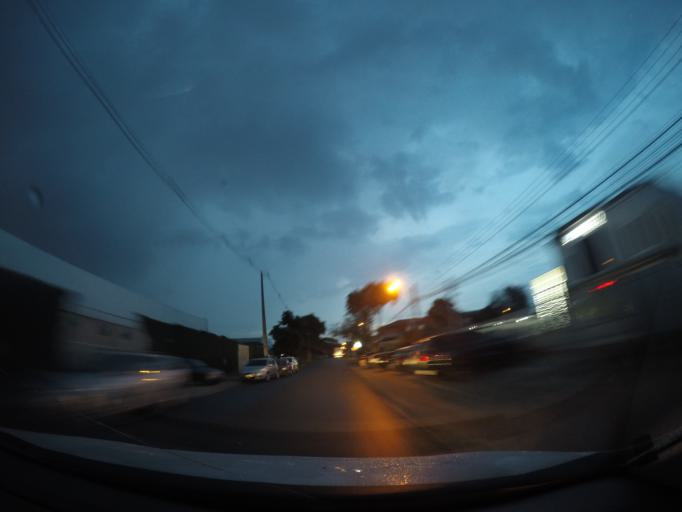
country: BR
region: Parana
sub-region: Sao Jose Dos Pinhais
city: Sao Jose dos Pinhais
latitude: -25.5151
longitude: -49.2269
